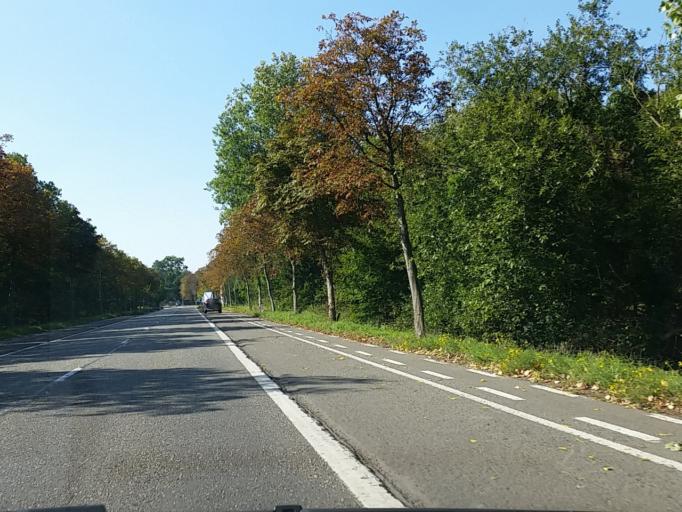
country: BE
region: Flanders
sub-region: Provincie Vlaams-Brabant
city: Machelen
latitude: 50.9226
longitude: 4.4566
